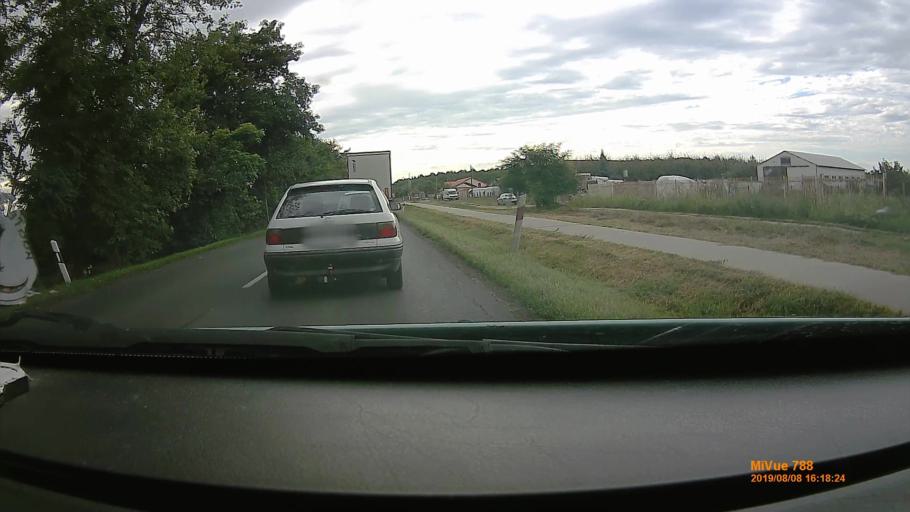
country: HU
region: Szabolcs-Szatmar-Bereg
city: Mateszalka
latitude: 47.9647
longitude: 22.2840
